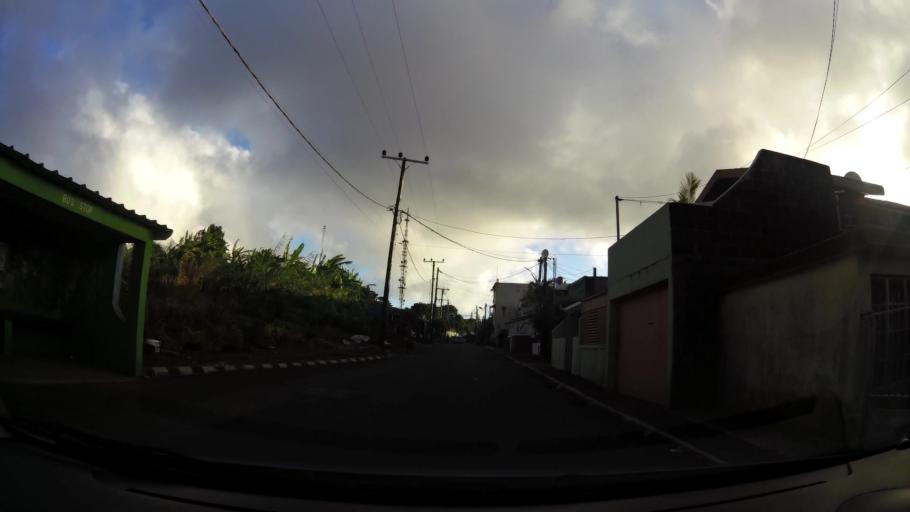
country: MU
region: Plaines Wilhems
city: Curepipe
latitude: -20.3103
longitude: 57.5373
